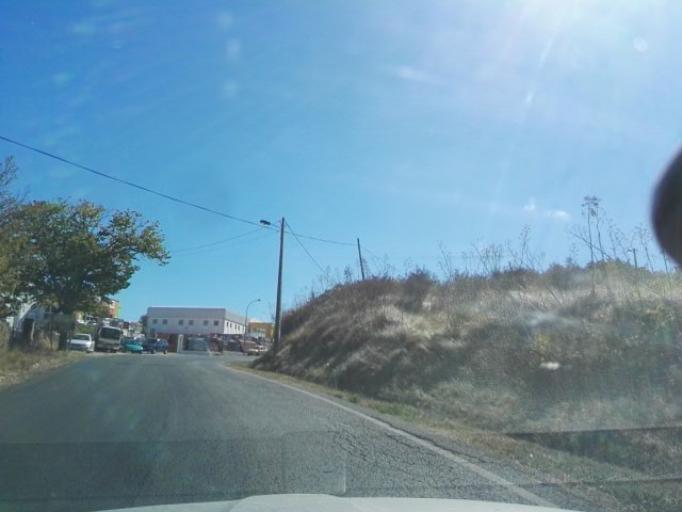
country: PT
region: Lisbon
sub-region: Arruda Dos Vinhos
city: Arruda dos Vinhos
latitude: 38.9772
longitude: -9.0748
